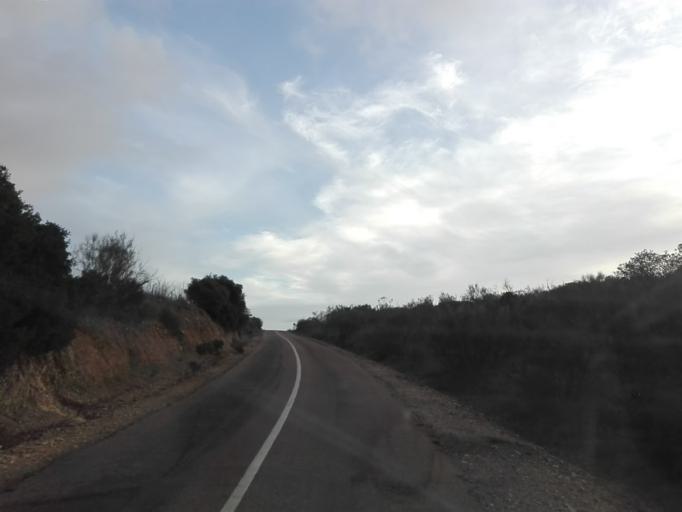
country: ES
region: Extremadura
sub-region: Provincia de Badajoz
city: Hinojosa del Valle
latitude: 38.4281
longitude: -6.1757
